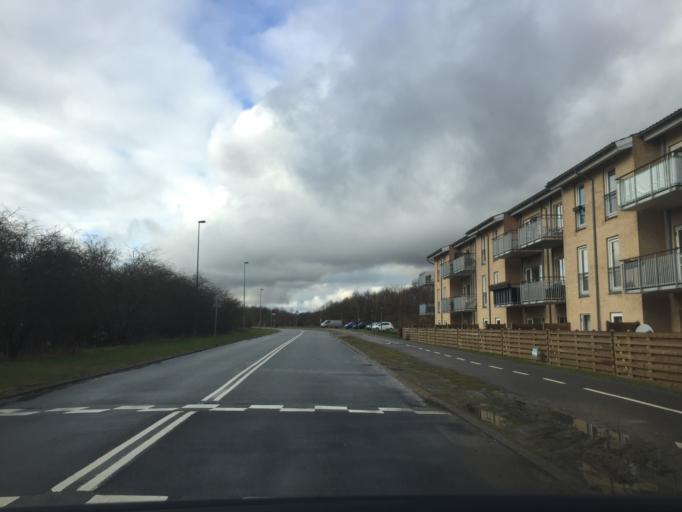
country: DK
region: Capital Region
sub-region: Fureso Kommune
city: Farum
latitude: 55.8199
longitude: 12.3528
